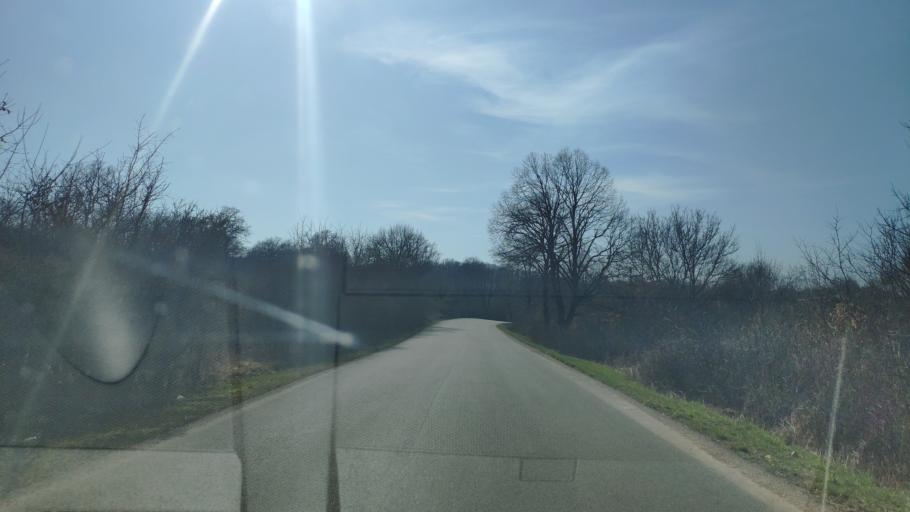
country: SK
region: Kosicky
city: Roznava
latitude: 48.5477
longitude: 20.3262
